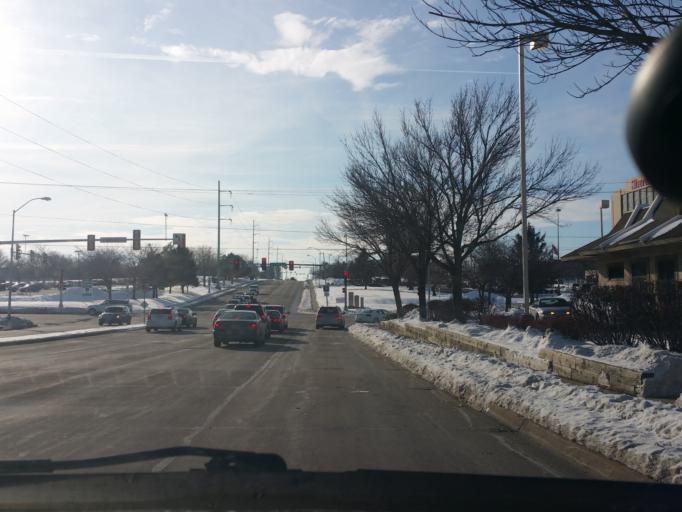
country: US
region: Iowa
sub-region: Polk County
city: Clive
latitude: 41.6012
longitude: -93.7715
